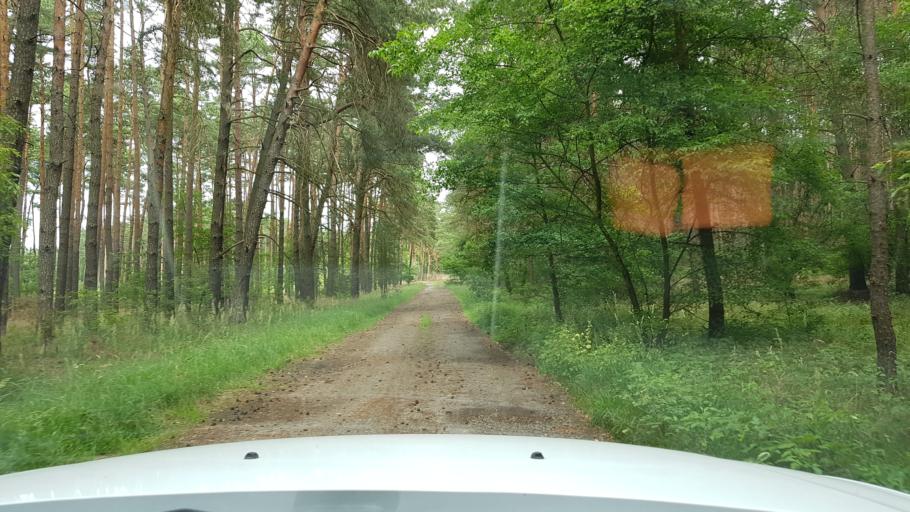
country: PL
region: West Pomeranian Voivodeship
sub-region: Powiat mysliborski
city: Boleszkowice
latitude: 52.6619
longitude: 14.5769
